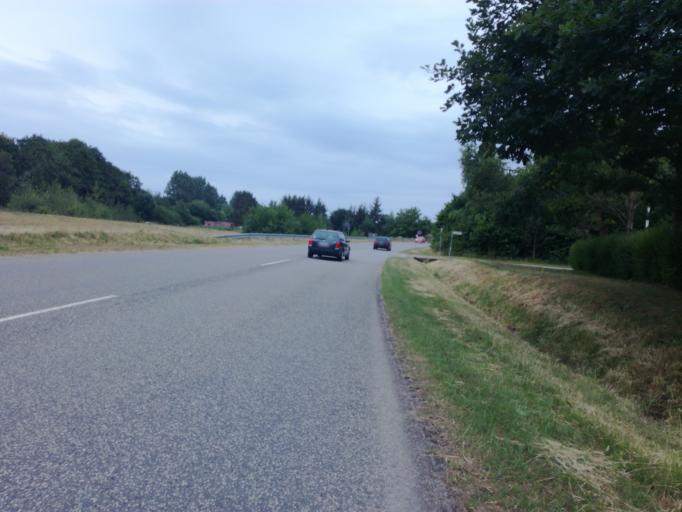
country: DK
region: South Denmark
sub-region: Vejle Kommune
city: Borkop
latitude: 55.6484
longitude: 9.6449
